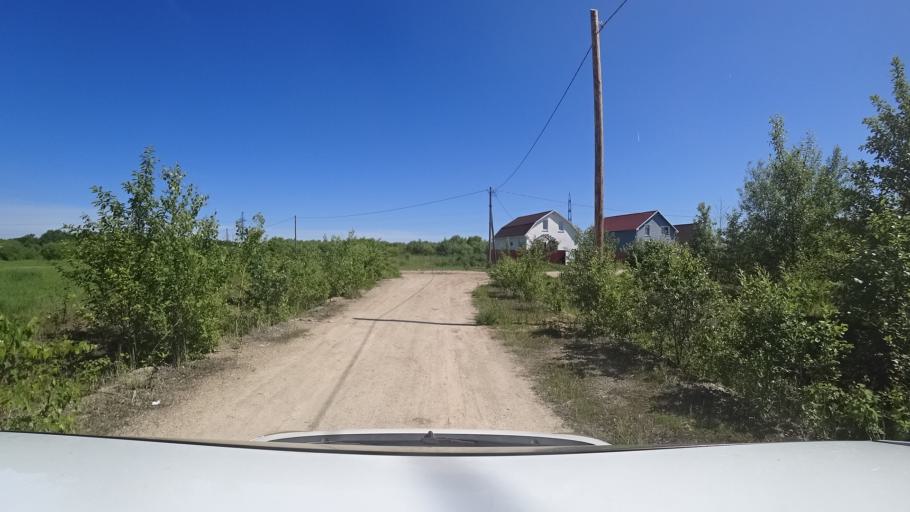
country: RU
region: Khabarovsk Krai
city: Topolevo
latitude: 48.5646
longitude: 135.1939
